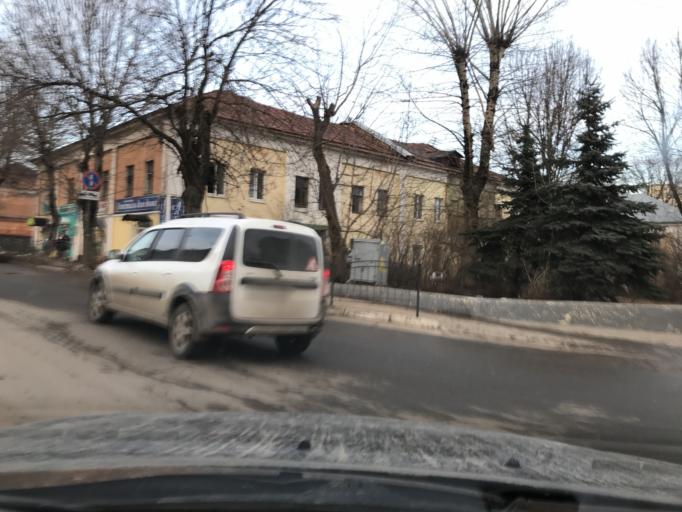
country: RU
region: Kaluga
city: Kaluga
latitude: 54.5113
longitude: 36.2447
